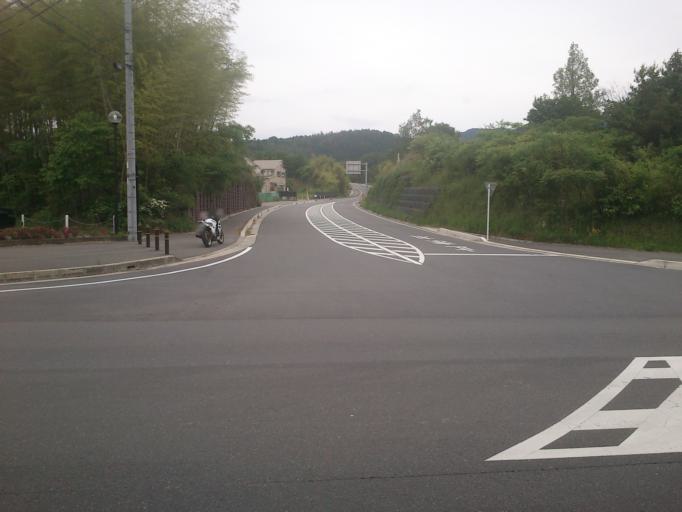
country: JP
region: Kyoto
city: Uji
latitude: 34.8448
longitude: 135.8421
